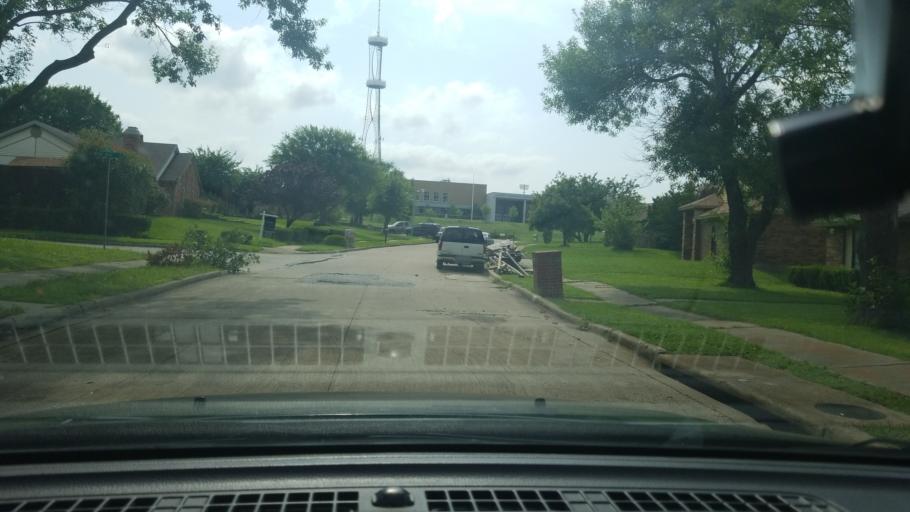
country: US
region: Texas
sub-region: Dallas County
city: Mesquite
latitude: 32.7626
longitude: -96.6296
